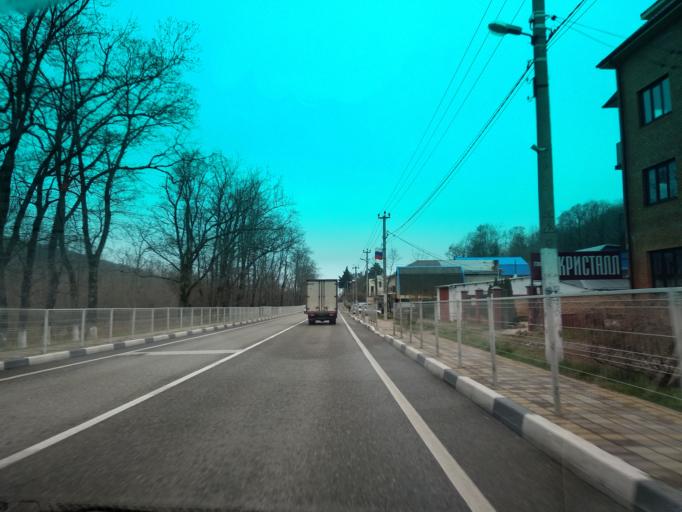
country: RU
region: Krasnodarskiy
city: Agoy
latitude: 44.1432
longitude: 39.0344
